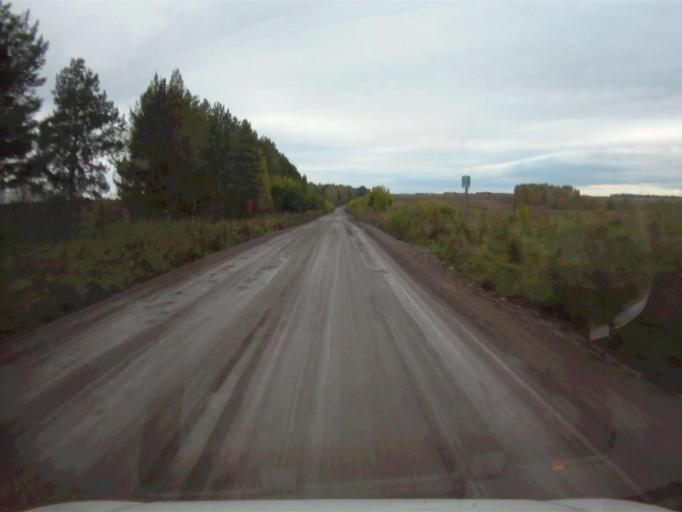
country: RU
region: Sverdlovsk
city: Mikhaylovsk
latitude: 56.1474
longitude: 59.2775
